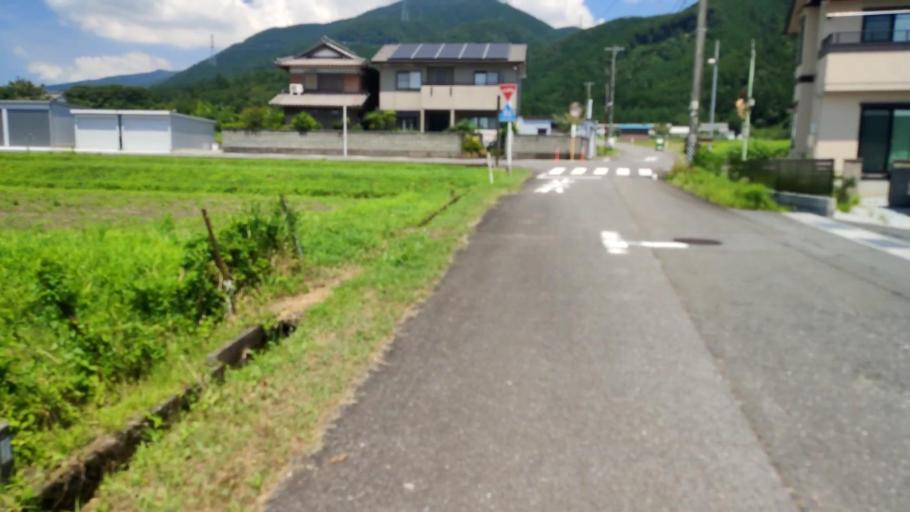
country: JP
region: Gifu
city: Tarui
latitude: 35.3685
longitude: 136.4625
